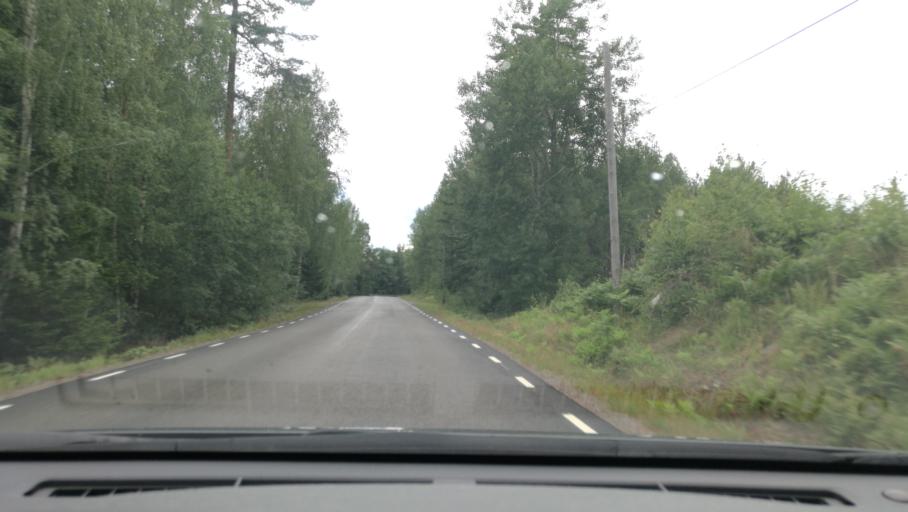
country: SE
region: OEstergoetland
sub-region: Norrkopings Kommun
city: Jursla
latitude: 58.8066
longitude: 16.1050
